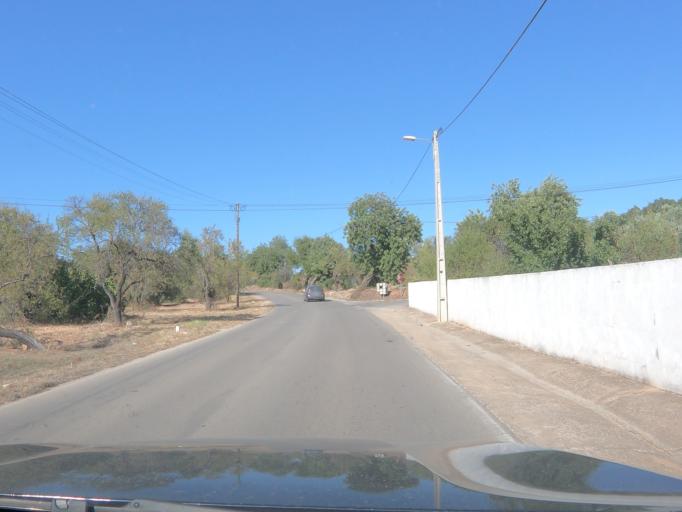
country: PT
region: Faro
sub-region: Loule
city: Almancil
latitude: 37.1118
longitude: -8.0289
